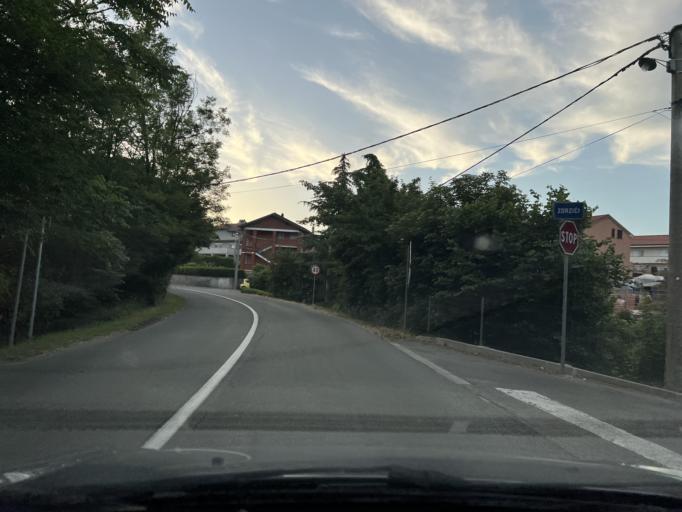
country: HR
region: Primorsko-Goranska
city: Marcelji
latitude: 45.3902
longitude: 14.4081
